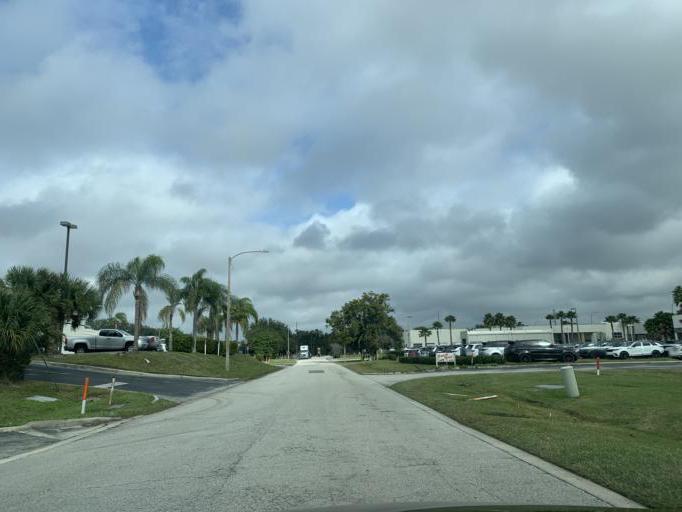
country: US
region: Florida
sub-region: Orange County
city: Eatonville
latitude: 28.6154
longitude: -81.3885
